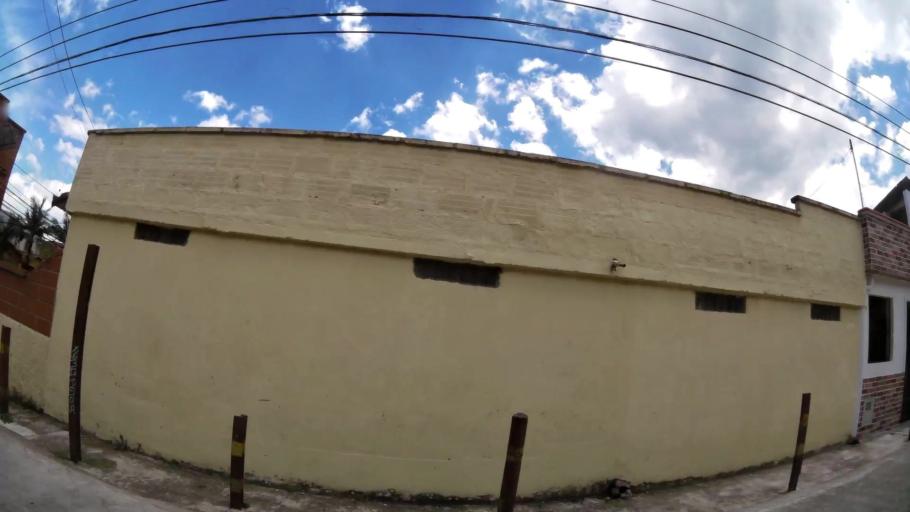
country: CO
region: Antioquia
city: La Estrella
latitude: 6.1609
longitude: -75.6454
